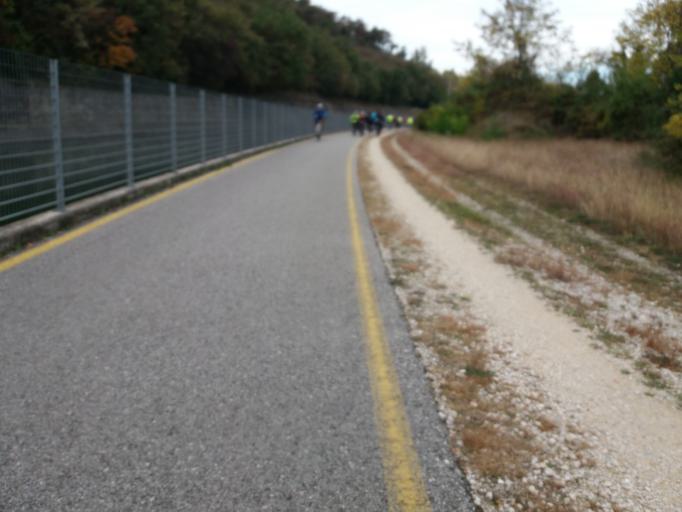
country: IT
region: Veneto
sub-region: Provincia di Verona
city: Pastrengo
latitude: 45.5014
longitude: 10.8044
